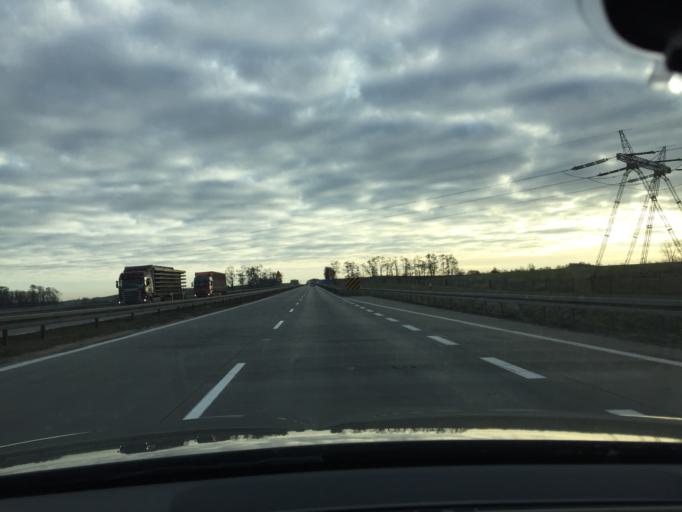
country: PL
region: Lower Silesian Voivodeship
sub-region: Powiat legnicki
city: Legnickie Pole
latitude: 51.1396
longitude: 16.2836
